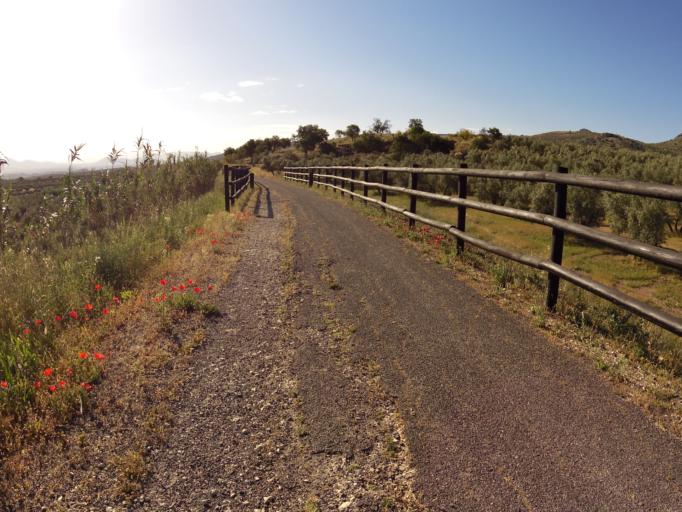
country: ES
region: Andalusia
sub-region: Province of Cordoba
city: Luque
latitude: 37.5695
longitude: -4.2535
